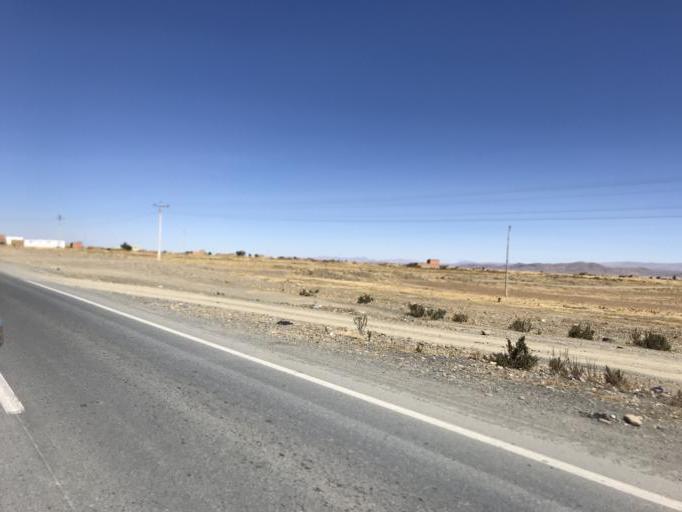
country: BO
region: La Paz
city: Batallas
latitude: -16.3302
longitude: -68.4218
